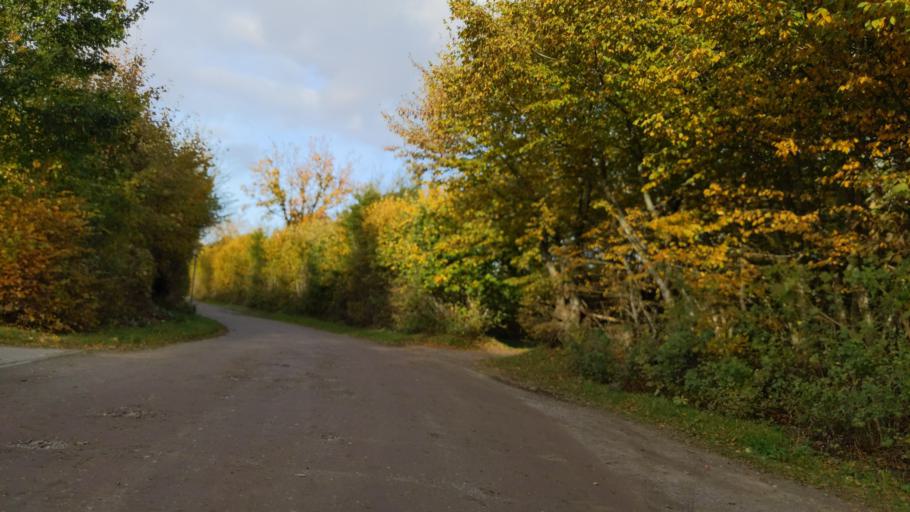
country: DE
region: Schleswig-Holstein
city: Eutin
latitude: 54.1483
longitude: 10.6293
